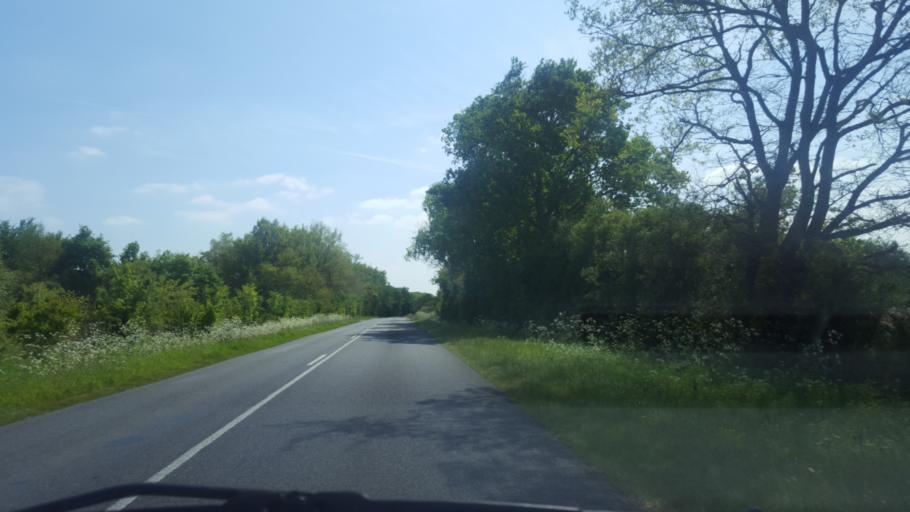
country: FR
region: Pays de la Loire
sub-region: Departement de la Loire-Atlantique
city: La Limouziniere
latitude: 46.9806
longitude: -1.5689
